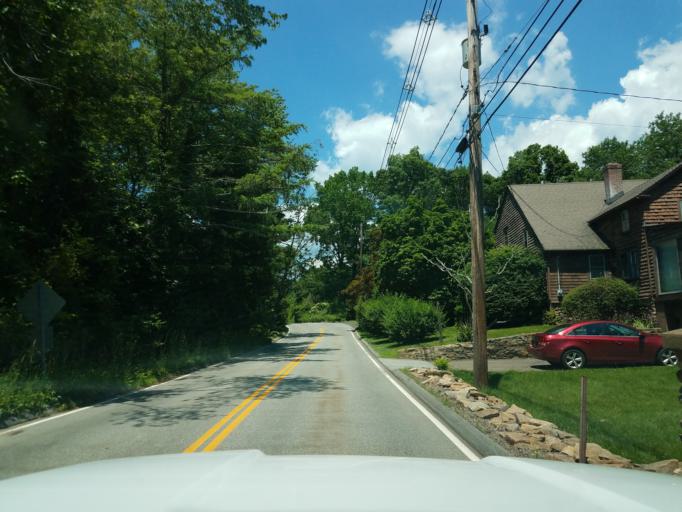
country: US
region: Connecticut
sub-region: New Haven County
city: Branford
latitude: 41.2785
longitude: -72.7728
